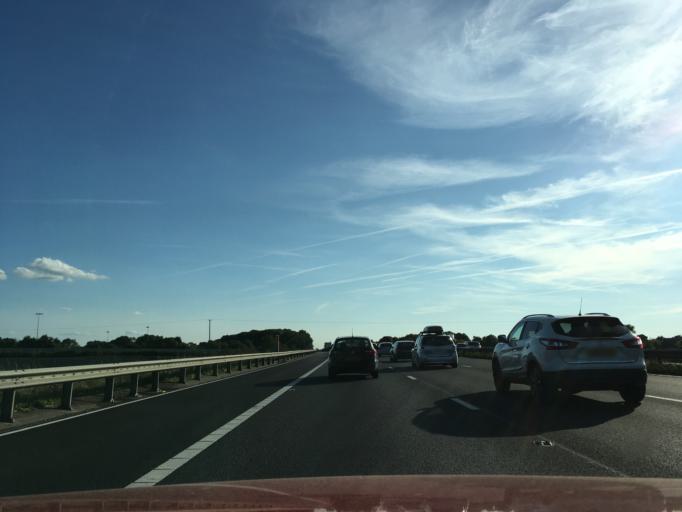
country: GB
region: England
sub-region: South Gloucestershire
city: Tytherington
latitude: 51.6016
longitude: -2.4792
